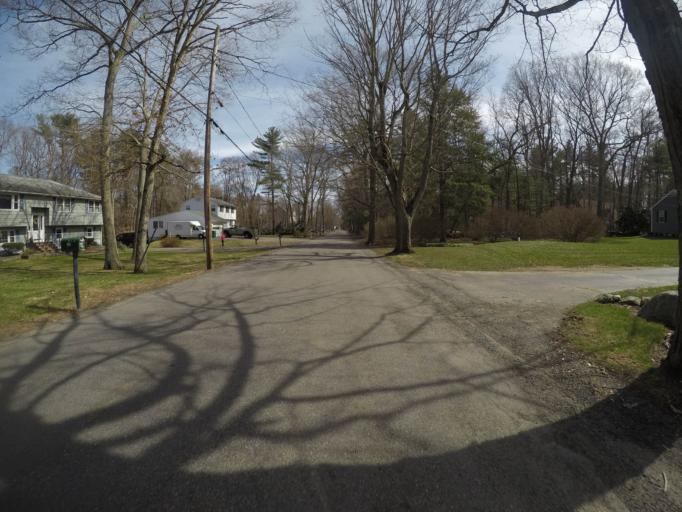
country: US
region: Massachusetts
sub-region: Bristol County
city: Easton
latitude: 42.0321
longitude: -71.0684
